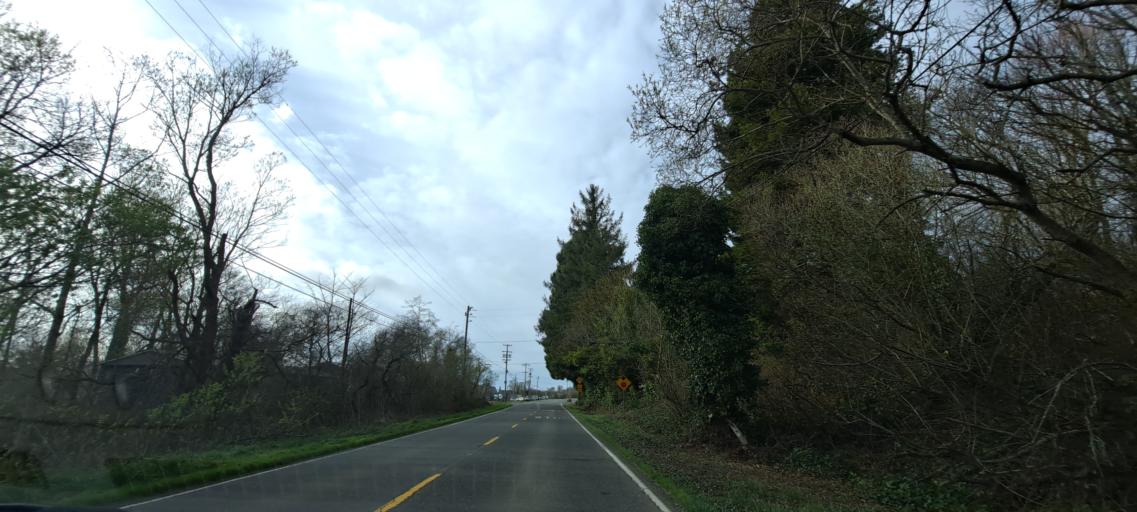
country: US
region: California
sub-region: Humboldt County
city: Fortuna
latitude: 40.6153
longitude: -124.1990
